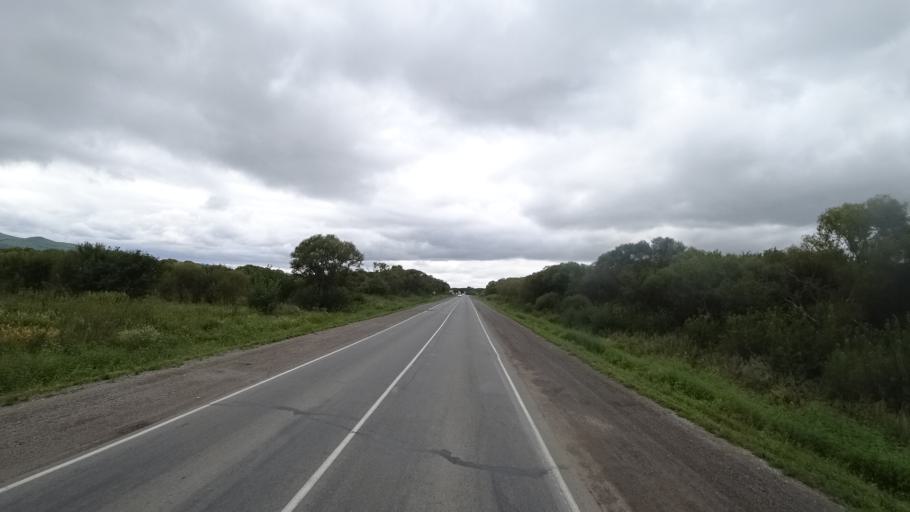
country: RU
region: Primorskiy
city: Chernigovka
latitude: 44.3454
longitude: 132.6037
